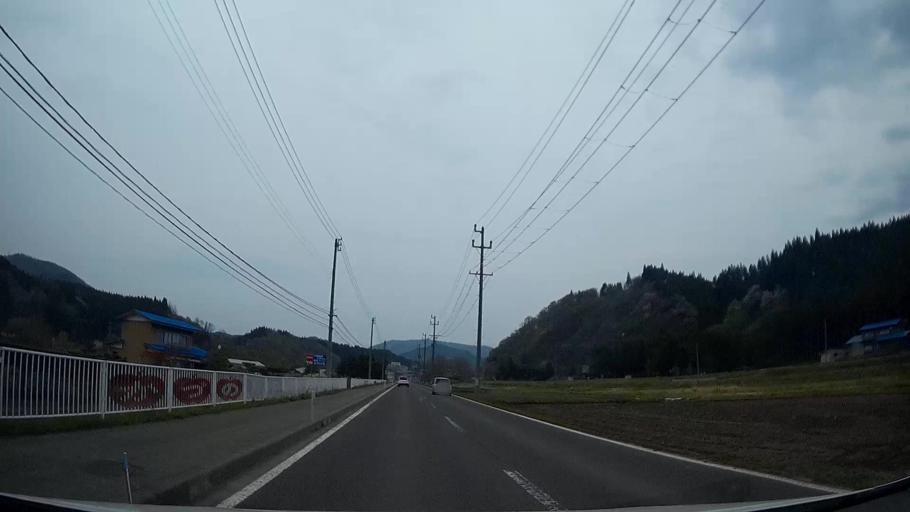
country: JP
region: Akita
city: Hanawa
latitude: 40.2903
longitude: 140.8134
